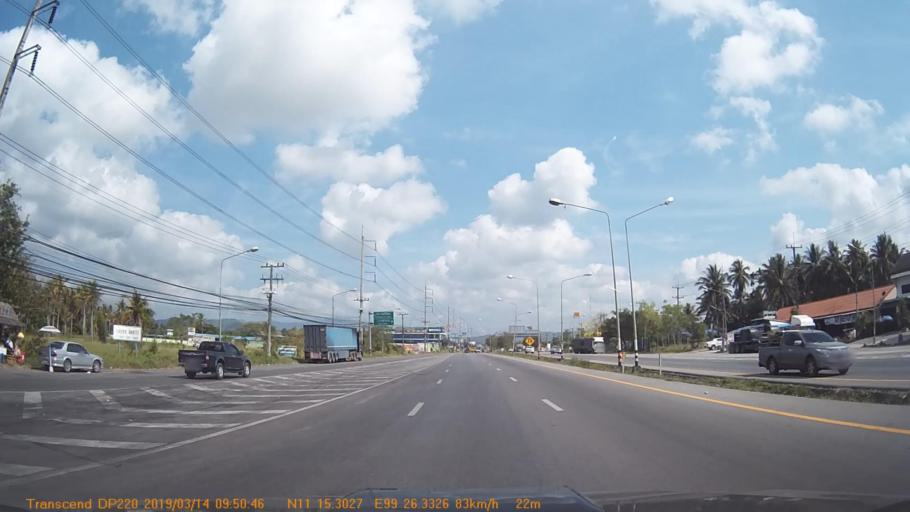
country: TH
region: Prachuap Khiri Khan
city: Bang Saphan
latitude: 11.2554
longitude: 99.4388
